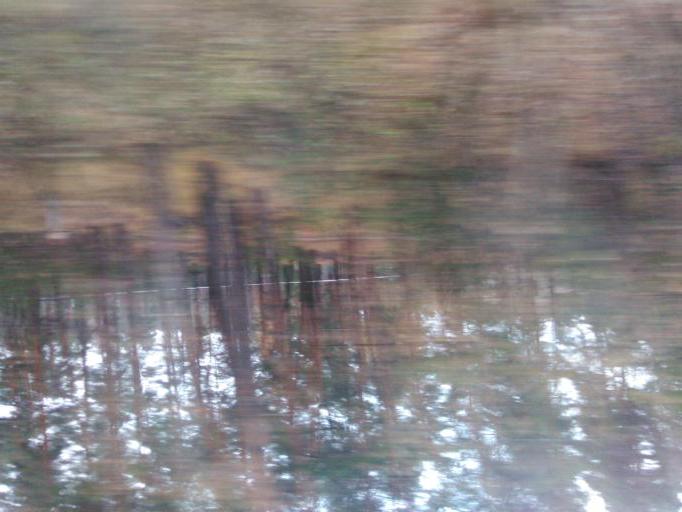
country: RU
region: Tatarstan
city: Osinovo
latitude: 55.8244
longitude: 48.8975
